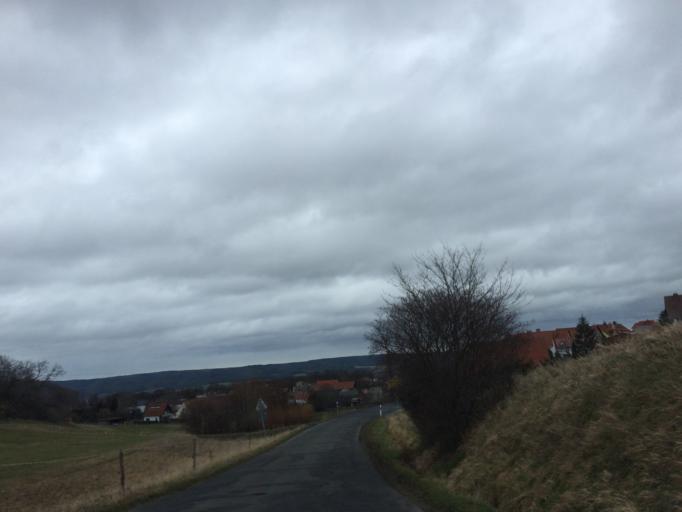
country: DE
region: Thuringia
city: Wernburg
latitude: 50.6749
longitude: 11.5954
